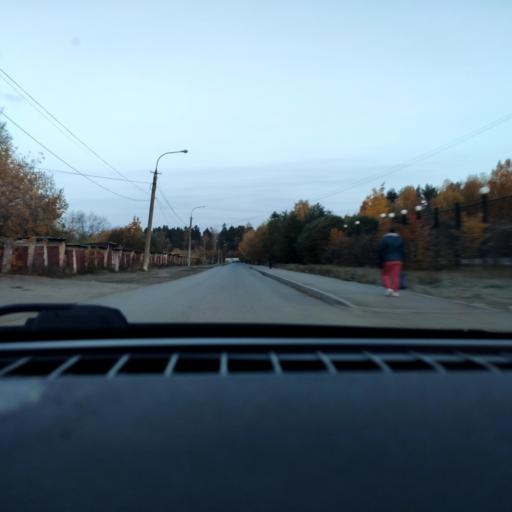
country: RU
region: Perm
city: Kondratovo
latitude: 57.9753
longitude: 56.1568
